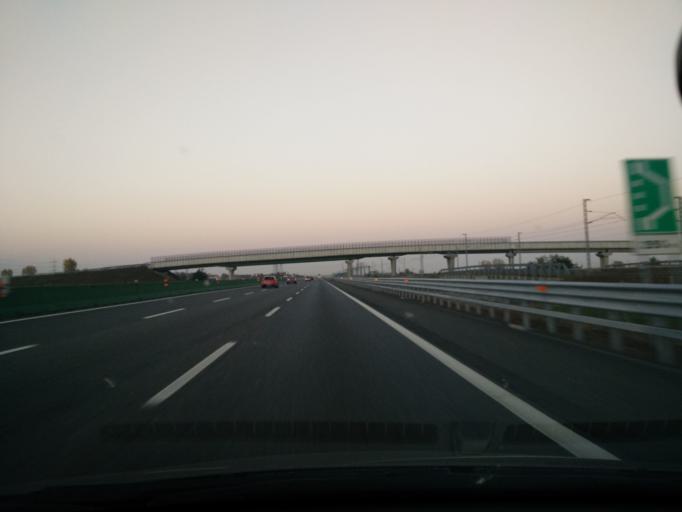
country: IT
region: Piedmont
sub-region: Provincia di Vercelli
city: Cigliano
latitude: 45.2752
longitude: 8.0229
